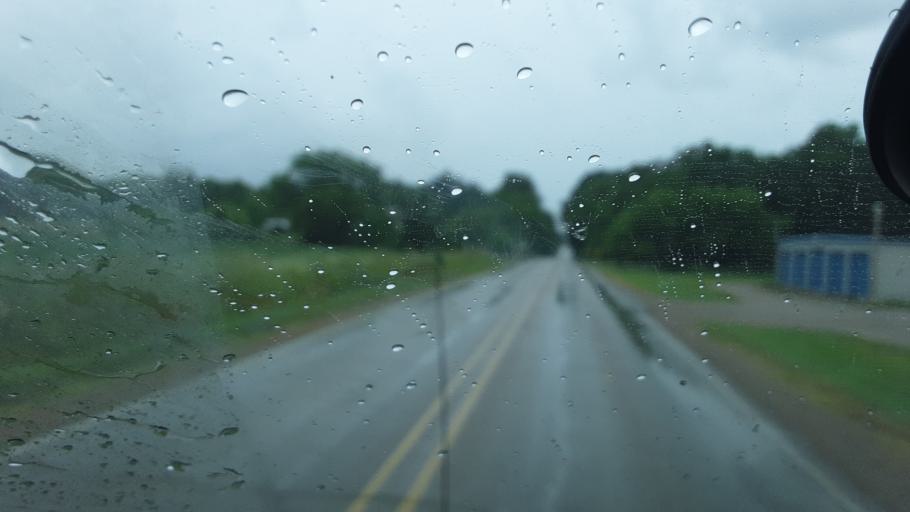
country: US
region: Ohio
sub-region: Williams County
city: Pioneer
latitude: 41.7089
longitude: -84.6320
